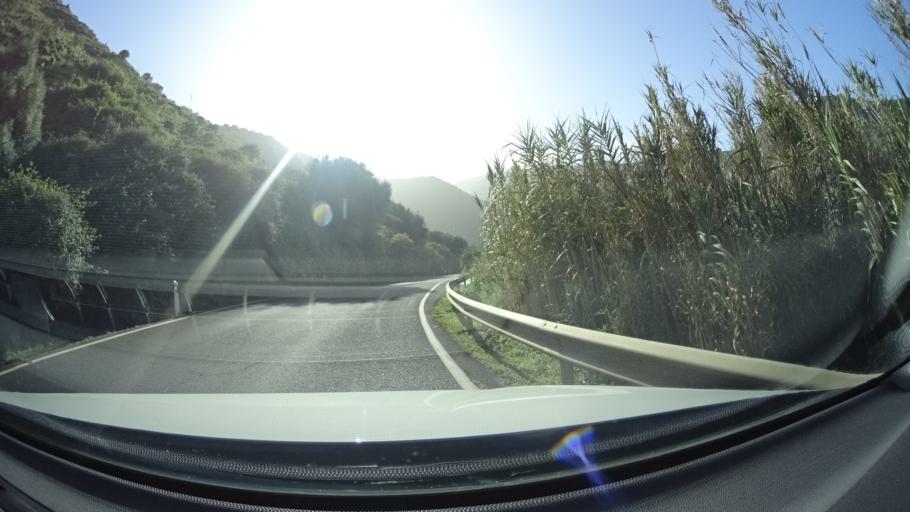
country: ES
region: Canary Islands
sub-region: Provincia de Las Palmas
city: Vega de San Mateo
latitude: 28.0177
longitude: -15.5464
